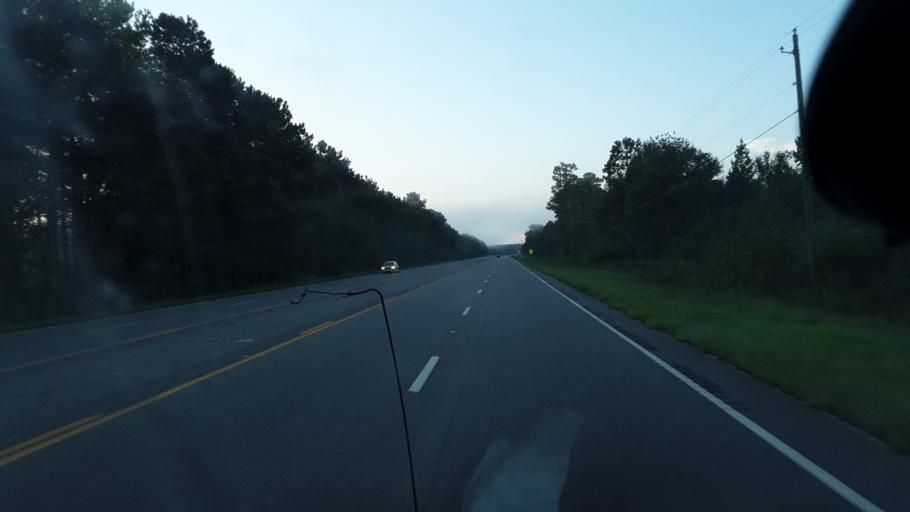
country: US
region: South Carolina
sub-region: Clarendon County
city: Manning
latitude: 33.7319
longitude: -80.2029
